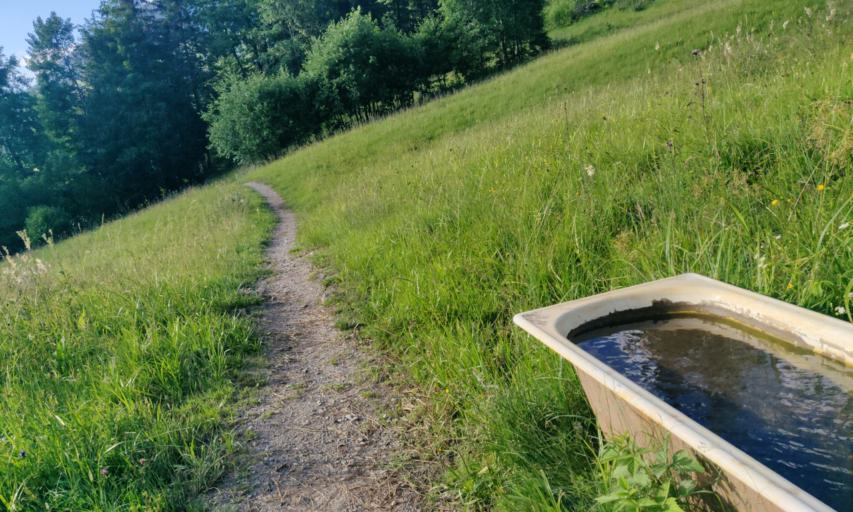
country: CH
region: Bern
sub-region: Obersimmental-Saanen District
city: Gstaad
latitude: 46.4089
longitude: 7.3393
